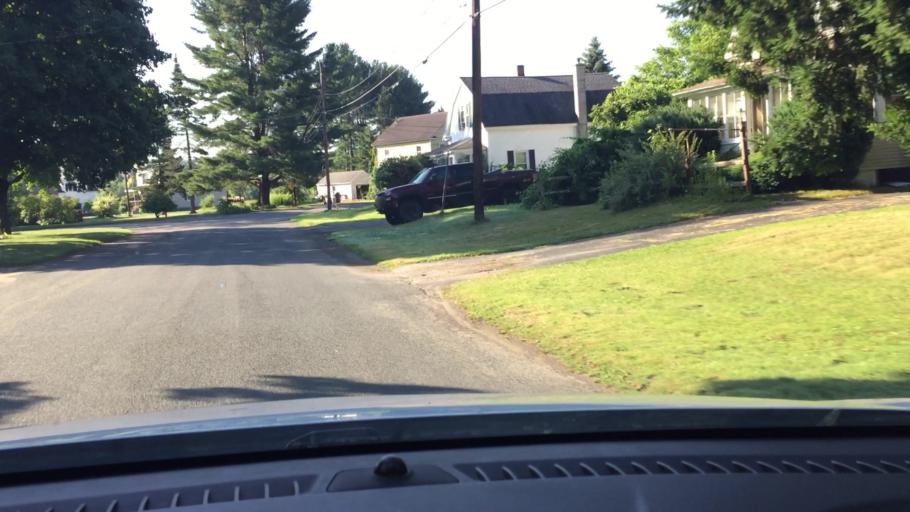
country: US
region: Massachusetts
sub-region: Berkshire County
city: Pittsfield
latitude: 42.4489
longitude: -73.2180
